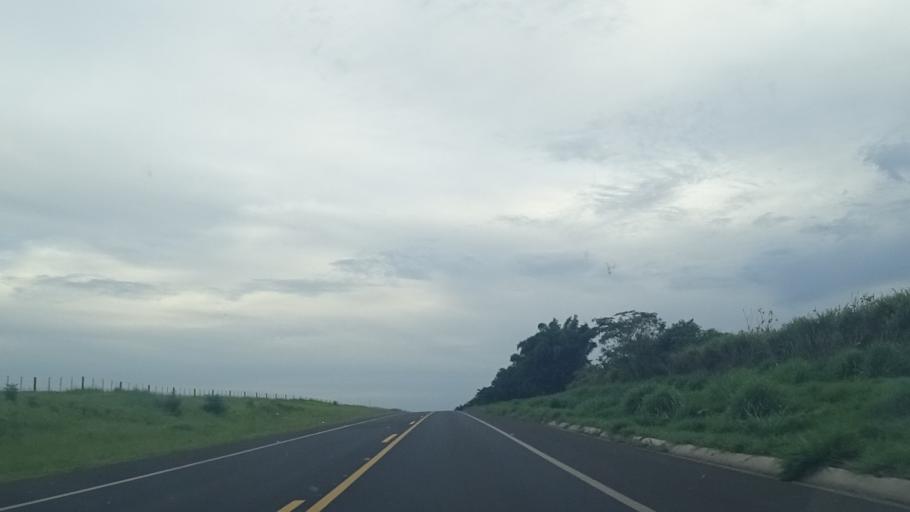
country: BR
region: Sao Paulo
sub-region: Martinopolis
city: Martinopolis
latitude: -22.0897
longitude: -51.1310
